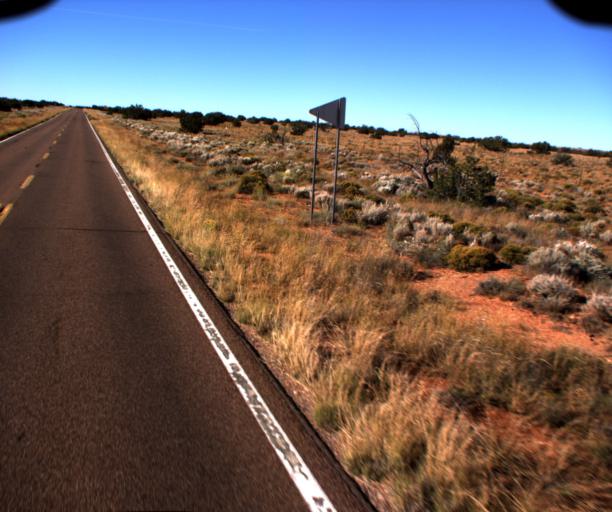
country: US
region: Arizona
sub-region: Navajo County
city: Holbrook
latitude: 34.6980
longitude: -110.3047
